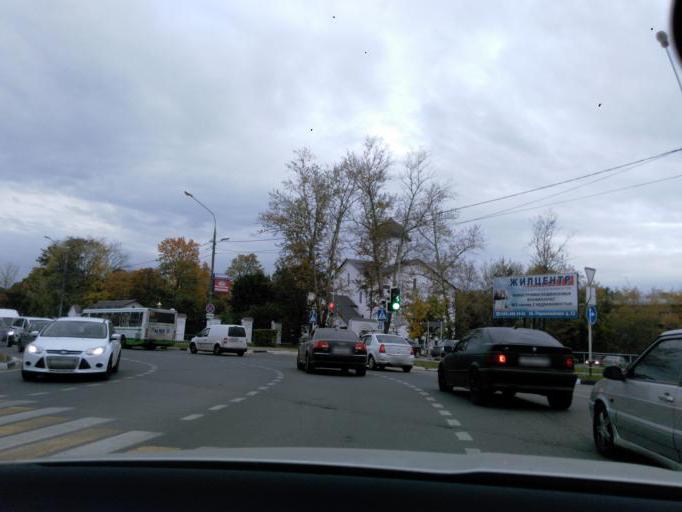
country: RU
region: Moskovskaya
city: Dolgoprudnyy
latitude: 55.9342
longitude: 37.5130
